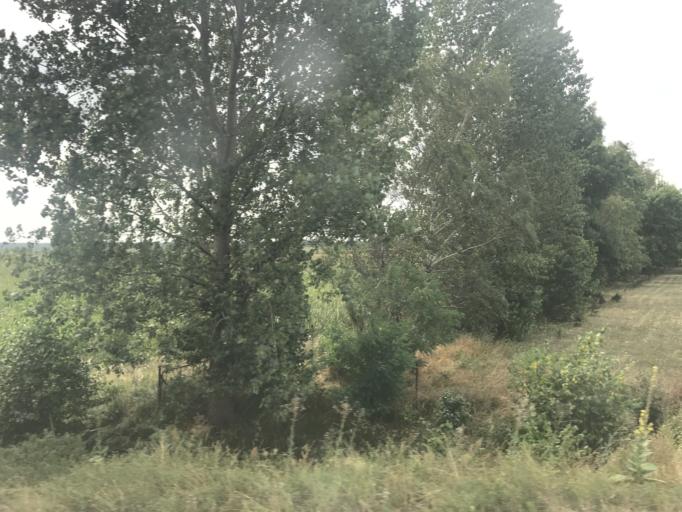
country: PL
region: Greater Poland Voivodeship
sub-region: Powiat poznanski
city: Pobiedziska
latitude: 52.4861
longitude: 17.3238
